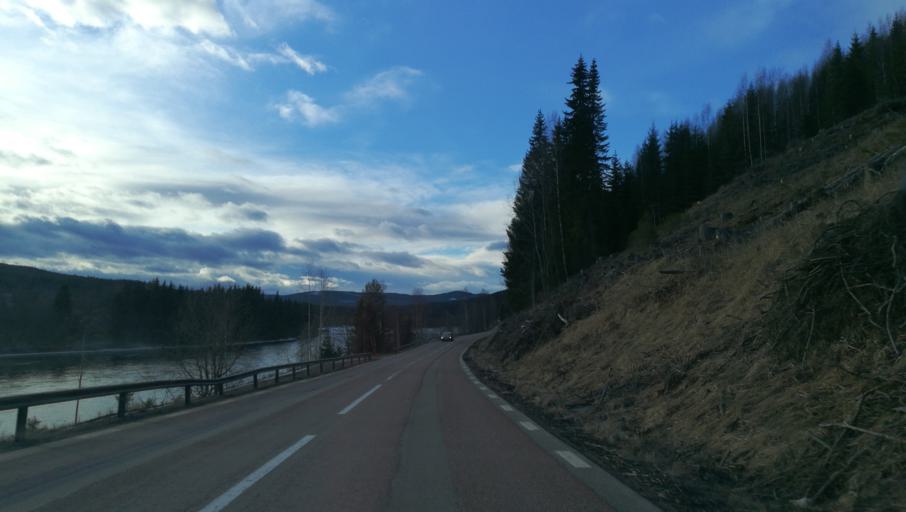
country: SE
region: Vaermland
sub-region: Torsby Kommun
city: Torsby
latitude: 60.7422
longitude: 12.8322
